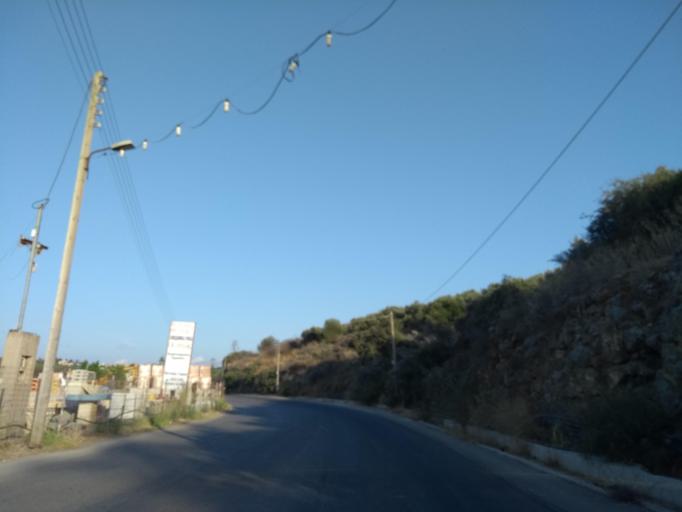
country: GR
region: Crete
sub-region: Nomos Chanias
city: Kalivai
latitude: 35.4192
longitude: 24.1879
